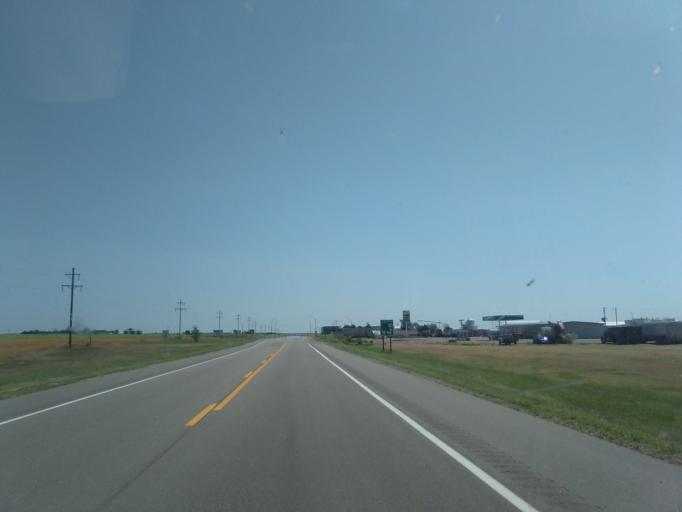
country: US
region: Nebraska
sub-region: Dundy County
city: Benkelman
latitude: 40.0591
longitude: -101.5356
